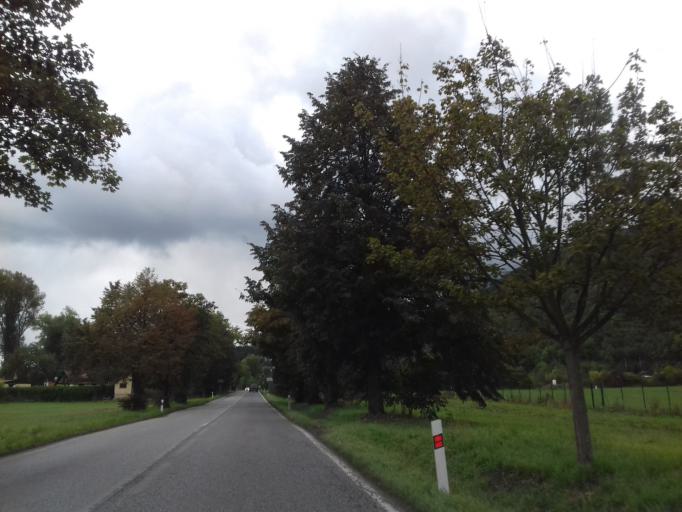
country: CZ
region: Central Bohemia
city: Cernosice
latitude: 49.9691
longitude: 14.3354
